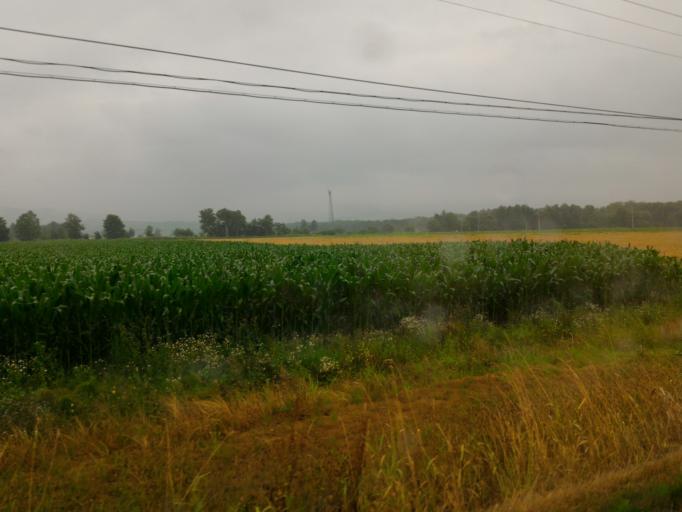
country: JP
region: Hokkaido
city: Nayoro
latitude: 44.5144
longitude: 142.3308
